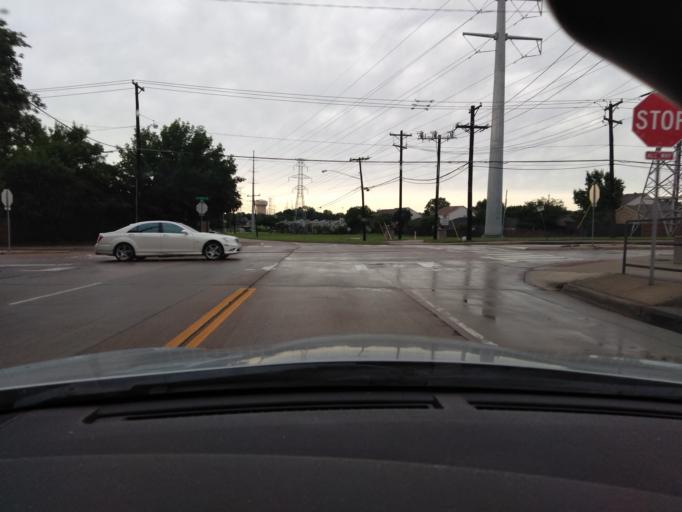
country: US
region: Texas
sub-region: Dallas County
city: Addison
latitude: 32.9878
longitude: -96.7786
